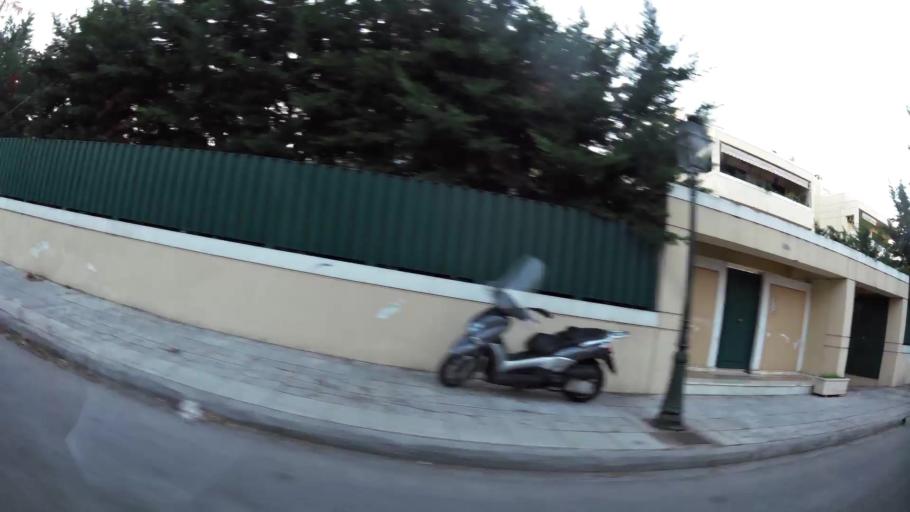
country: GR
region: Attica
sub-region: Nomarchia Athinas
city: Kifisia
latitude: 38.0775
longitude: 23.8206
